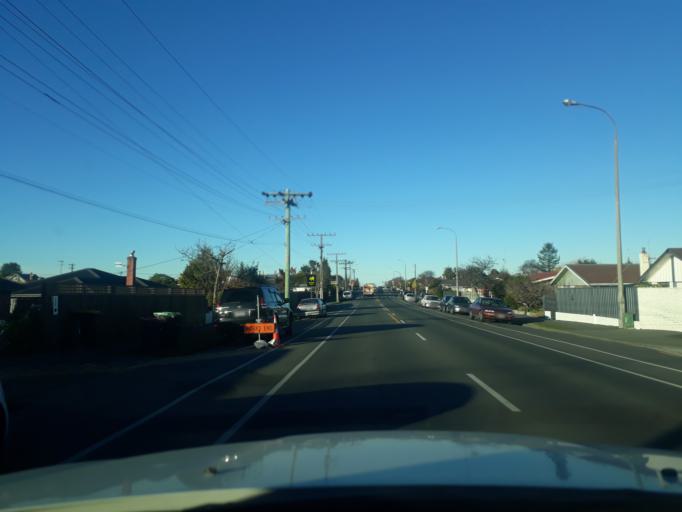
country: NZ
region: Canterbury
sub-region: Timaru District
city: Timaru
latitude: -44.3891
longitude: 171.2126
